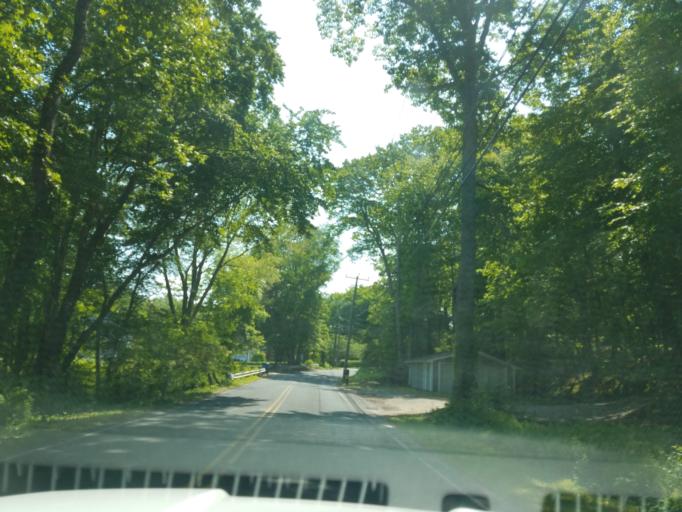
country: US
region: Connecticut
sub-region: New London County
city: Montville Center
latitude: 41.4961
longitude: -72.2136
